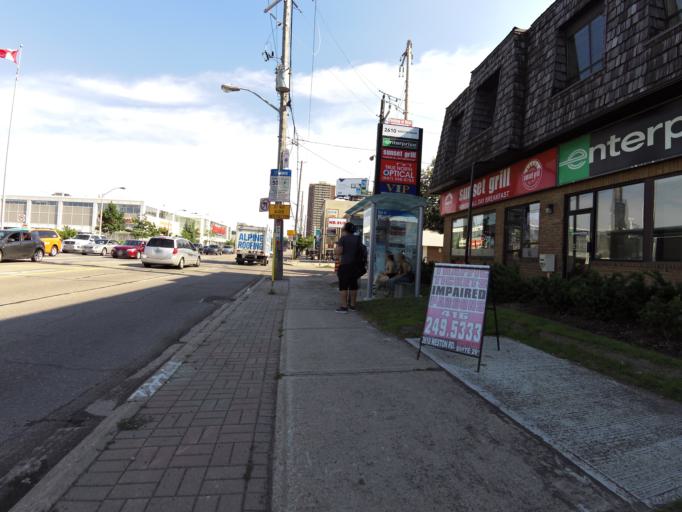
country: CA
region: Ontario
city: Etobicoke
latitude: 43.7115
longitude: -79.5354
